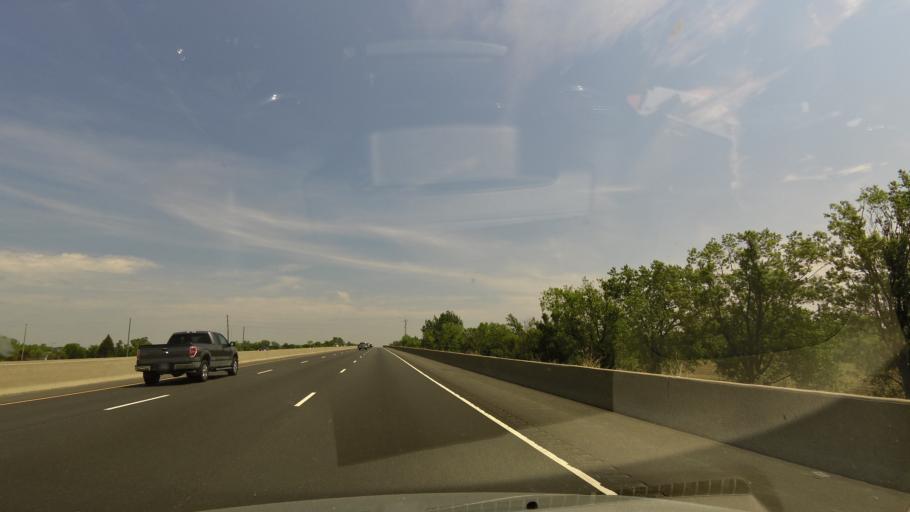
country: CA
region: Ontario
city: Oshawa
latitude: 43.9135
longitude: -78.5709
